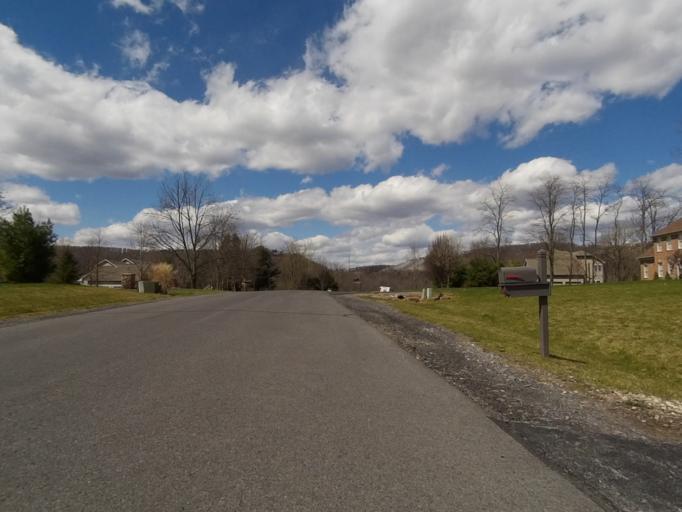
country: US
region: Pennsylvania
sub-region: Centre County
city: Park Forest Village
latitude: 40.8236
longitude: -77.9557
